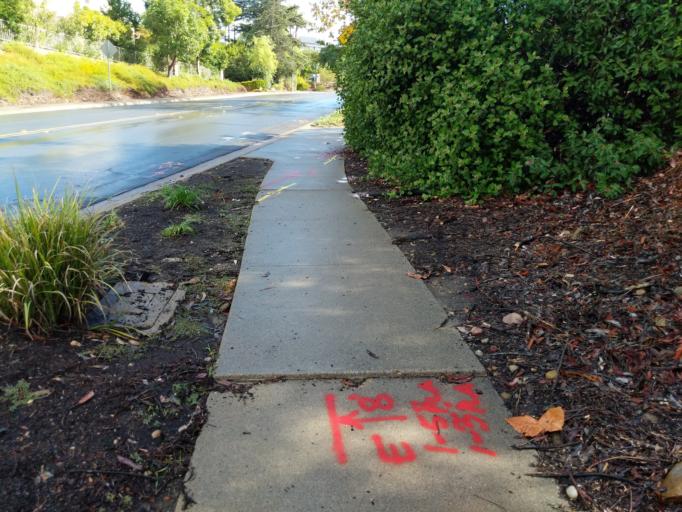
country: US
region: California
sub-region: San Diego County
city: Poway
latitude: 32.9061
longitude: -117.0729
